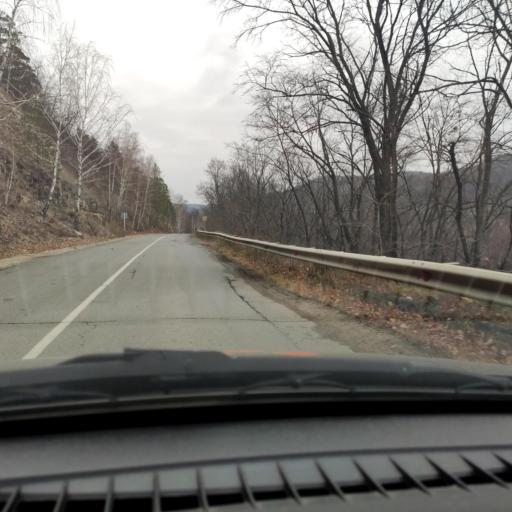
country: RU
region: Samara
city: Povolzhskiy
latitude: 53.4354
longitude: 49.6697
